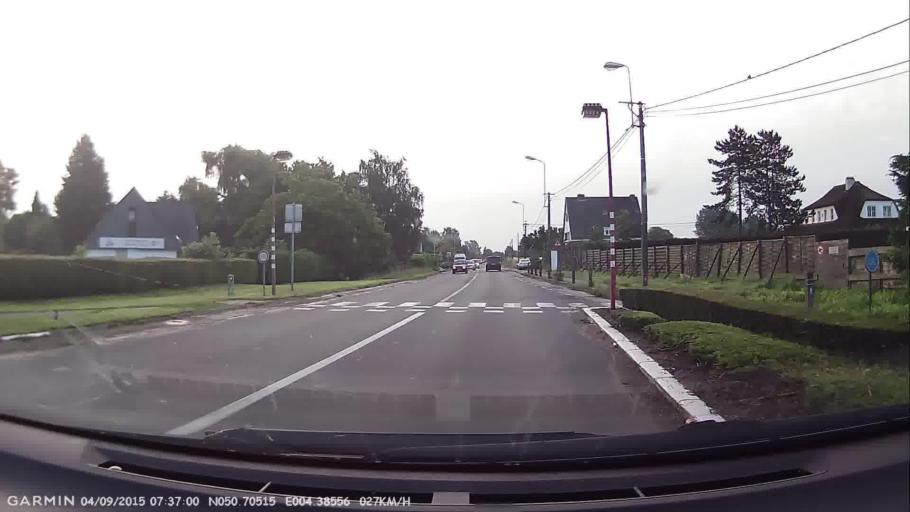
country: BE
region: Wallonia
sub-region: Province du Brabant Wallon
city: Waterloo
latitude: 50.7051
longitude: 4.3858
